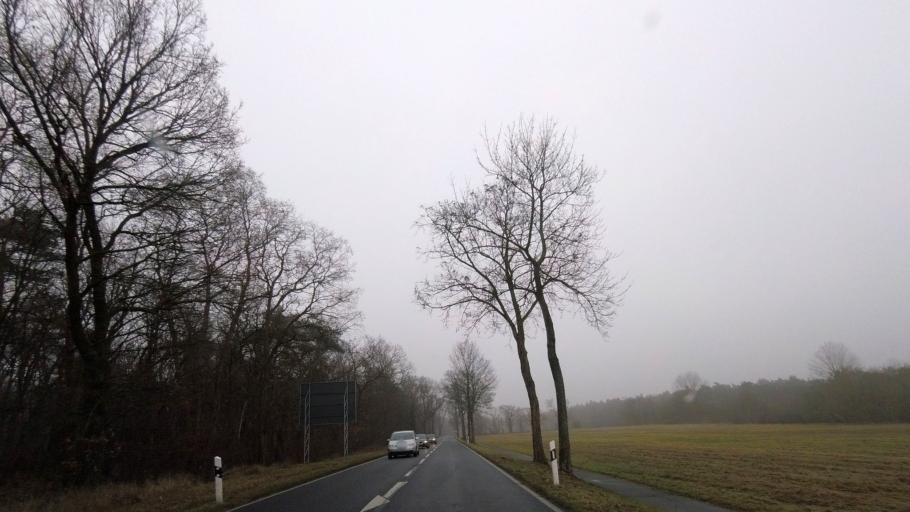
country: DE
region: Brandenburg
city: Juterbog
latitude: 51.9980
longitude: 13.0343
